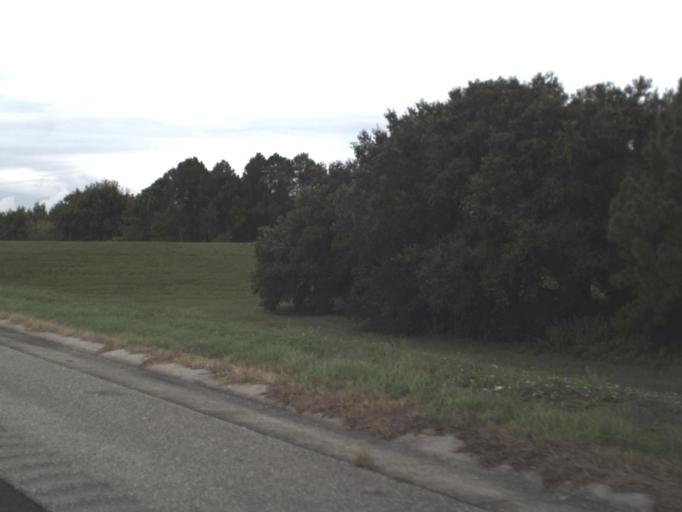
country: US
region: Florida
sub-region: Sarasota County
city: Fruitville
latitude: 27.3407
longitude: -82.4470
